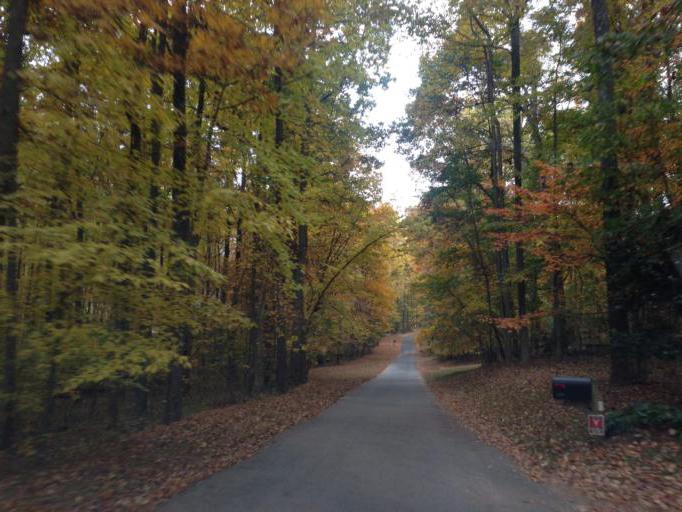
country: US
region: Maryland
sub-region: Howard County
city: Highland
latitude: 39.2540
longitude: -76.9738
